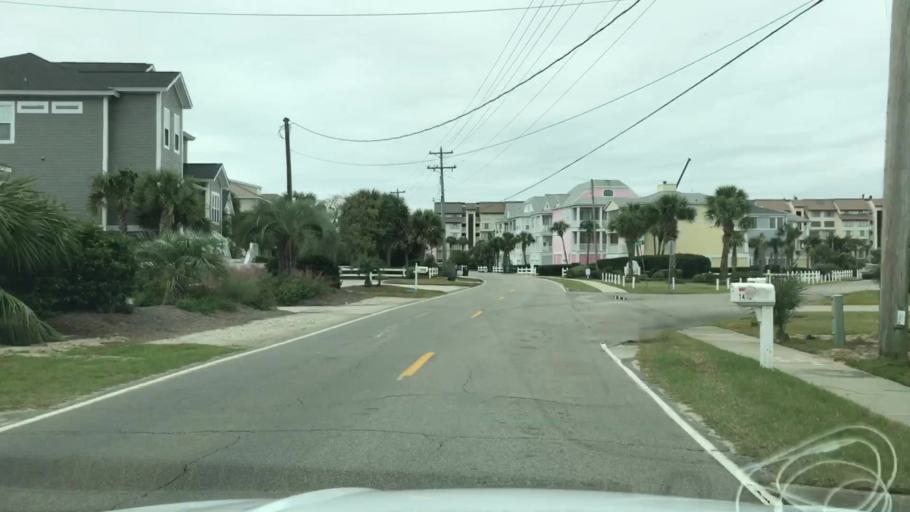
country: US
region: South Carolina
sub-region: Georgetown County
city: Murrells Inlet
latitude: 33.5544
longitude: -79.0173
